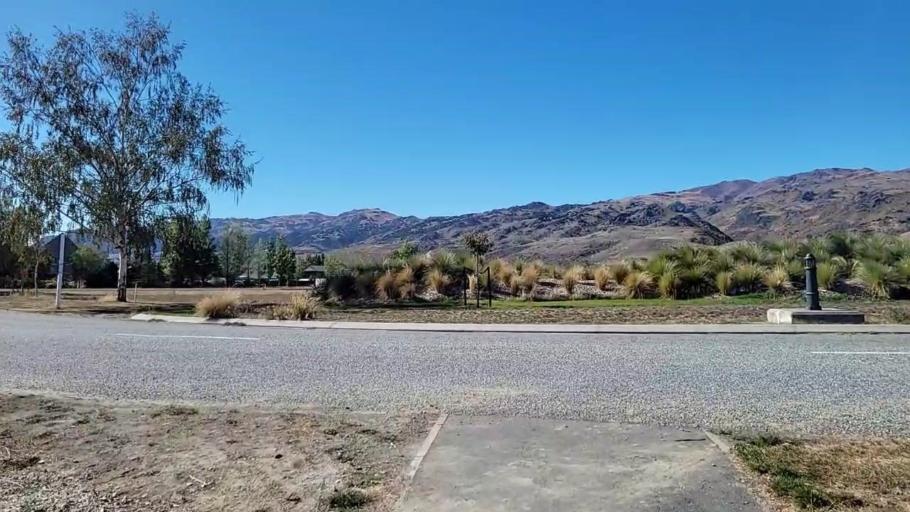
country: NZ
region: Otago
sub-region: Queenstown-Lakes District
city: Wanaka
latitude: -44.9771
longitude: 169.2391
